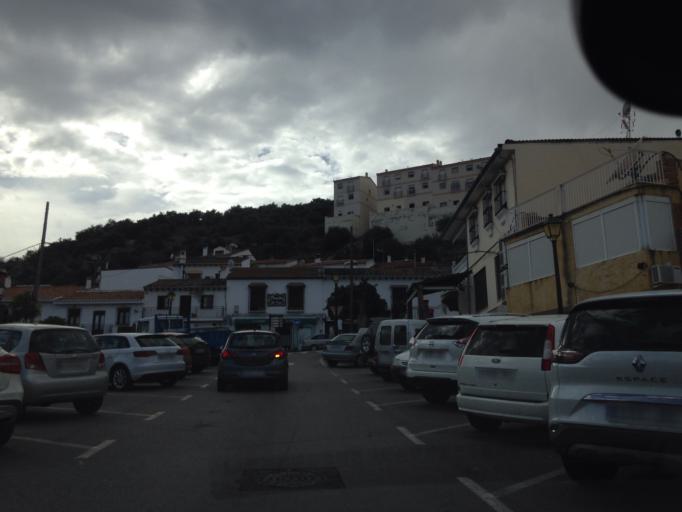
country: ES
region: Andalusia
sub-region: Provincia de Malaga
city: Casabermeja
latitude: 36.8952
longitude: -4.4311
